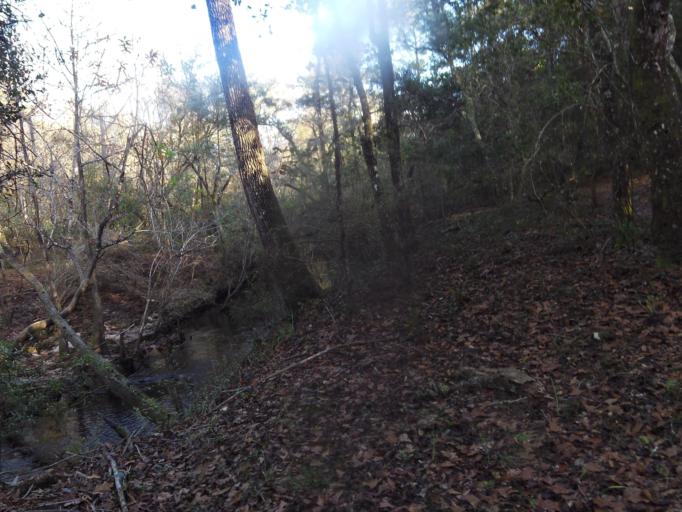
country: US
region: Florida
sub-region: Clay County
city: Middleburg
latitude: 30.1418
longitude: -81.9374
